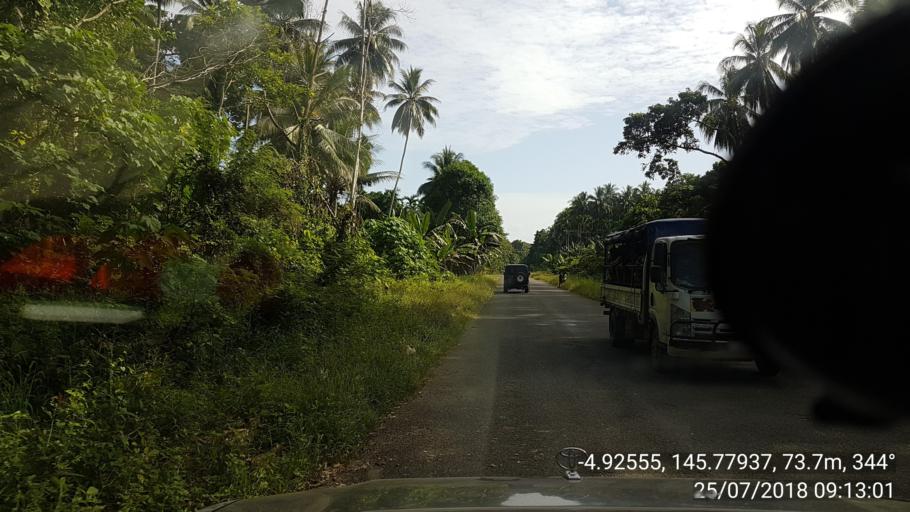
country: PG
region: Madang
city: Madang
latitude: -4.9256
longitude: 145.7794
